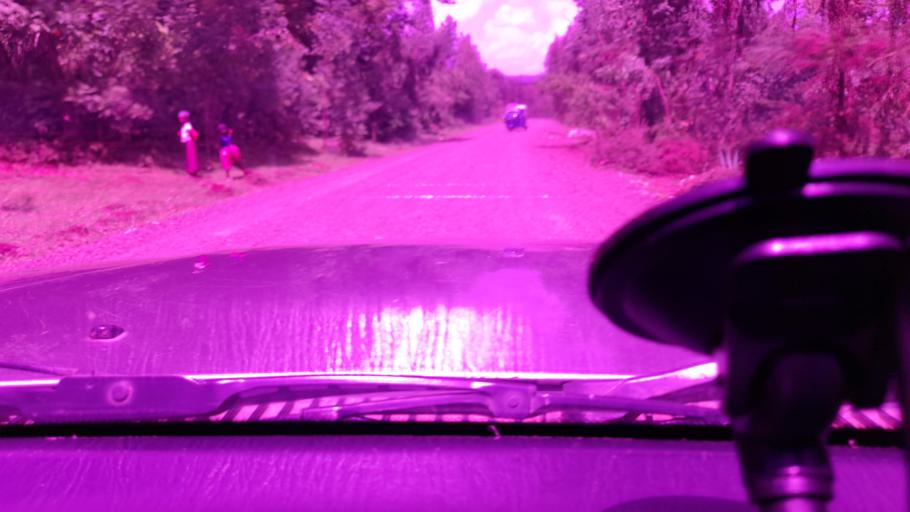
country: ET
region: Oromiya
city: Jima
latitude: 7.9935
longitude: 37.4791
